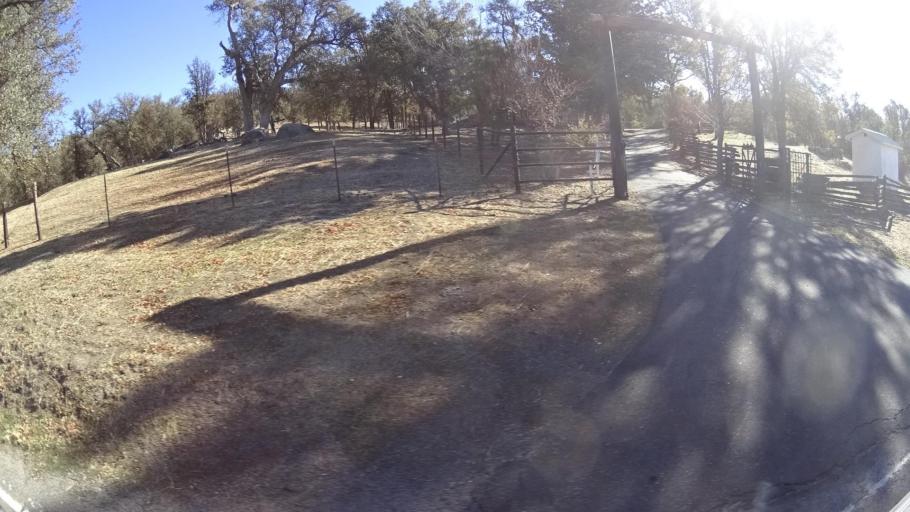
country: US
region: California
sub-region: Kern County
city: Alta Sierra
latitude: 35.7311
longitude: -118.7221
